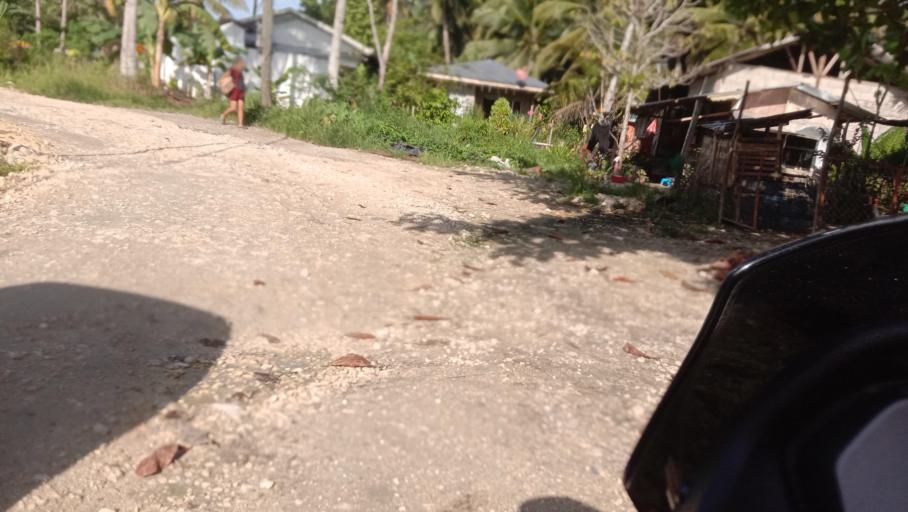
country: PH
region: Caraga
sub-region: Province of Agusan del Sur
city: Alegria
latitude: 8.4805
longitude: 125.9643
